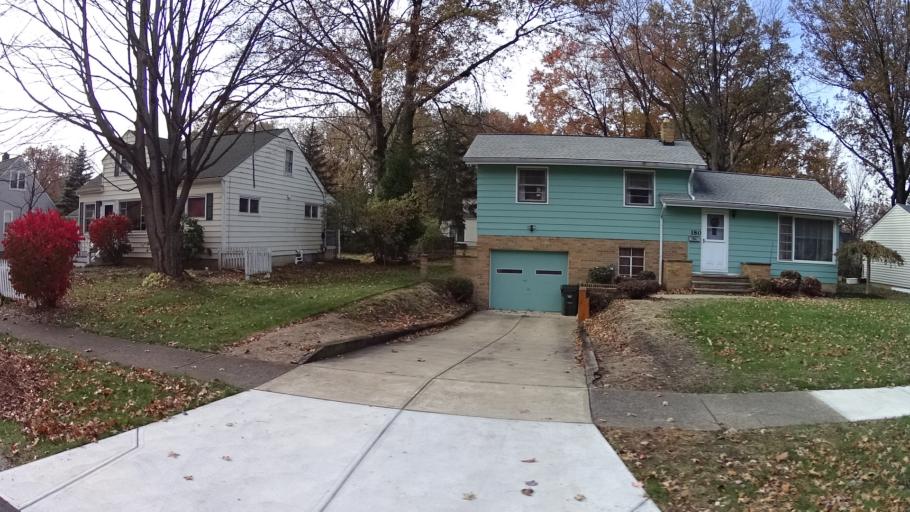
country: US
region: Ohio
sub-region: Lorain County
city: Avon Lake
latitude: 41.5076
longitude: -82.0236
